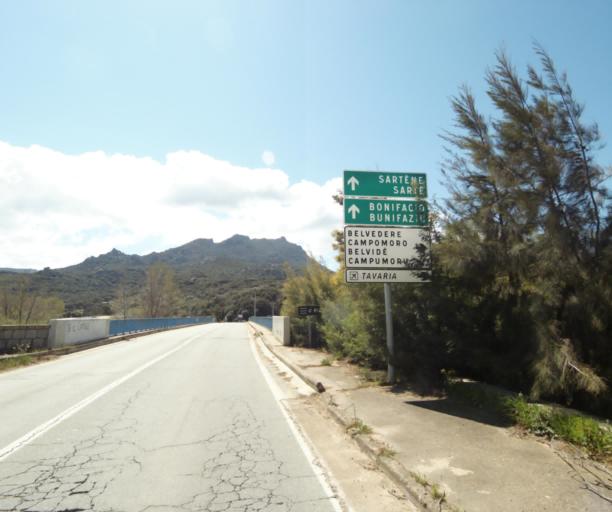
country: FR
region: Corsica
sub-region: Departement de la Corse-du-Sud
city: Propriano
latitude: 41.6580
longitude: 8.9175
